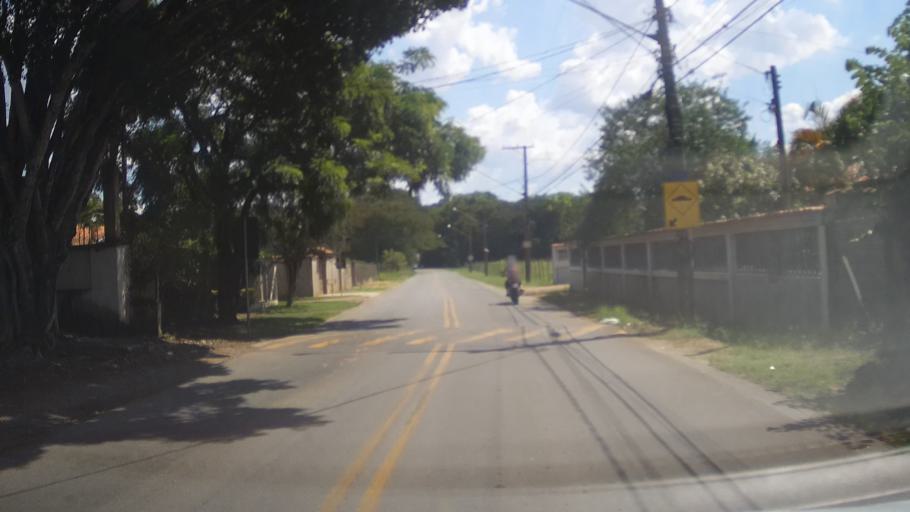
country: BR
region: Sao Paulo
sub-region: Varzea Paulista
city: Varzea Paulista
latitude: -23.1464
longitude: -46.8326
